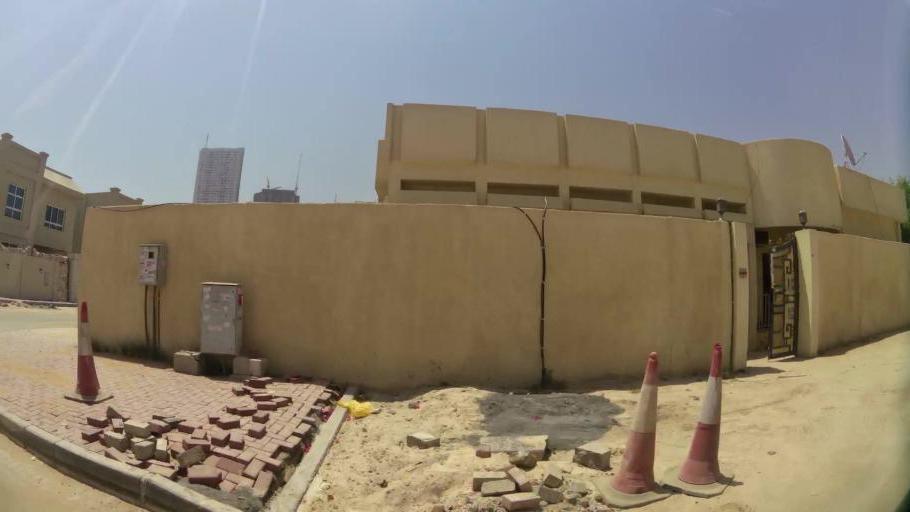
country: AE
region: Ajman
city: Ajman
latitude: 25.4022
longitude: 55.4357
